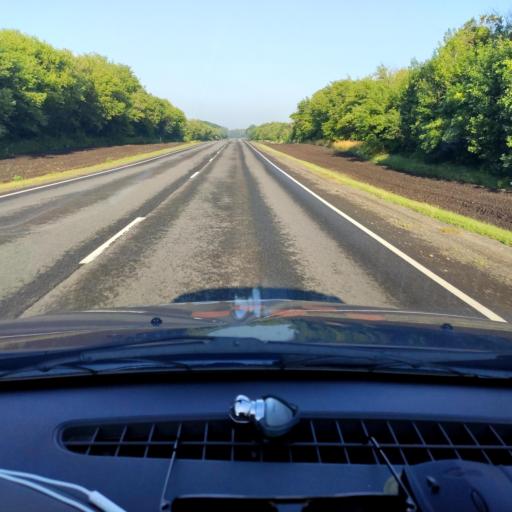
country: RU
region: Orjol
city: Livny
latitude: 52.4352
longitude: 37.8752
